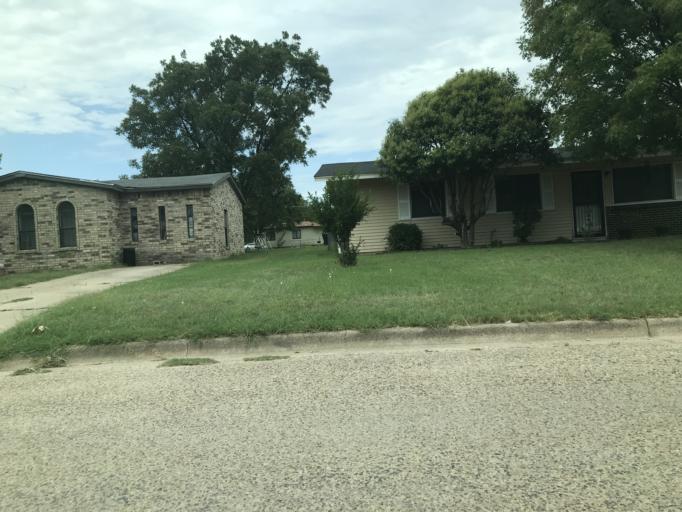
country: US
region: Texas
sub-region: Taylor County
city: Abilene
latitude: 32.4501
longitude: -99.6966
